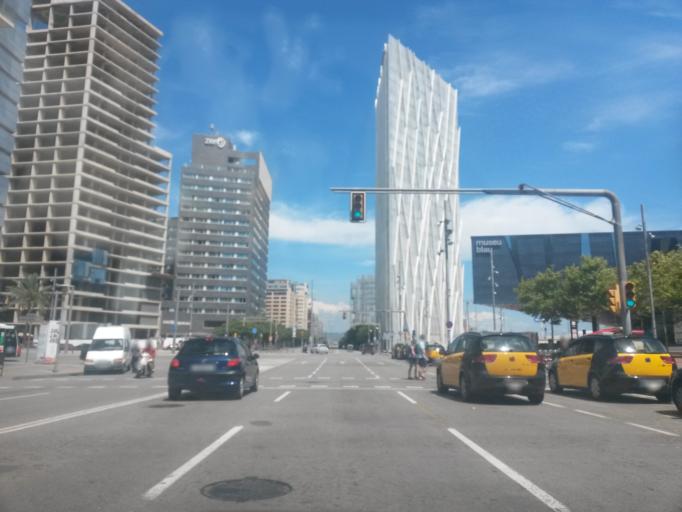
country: ES
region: Catalonia
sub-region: Provincia de Barcelona
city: Sant Adria de Besos
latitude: 41.4108
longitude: 2.2189
